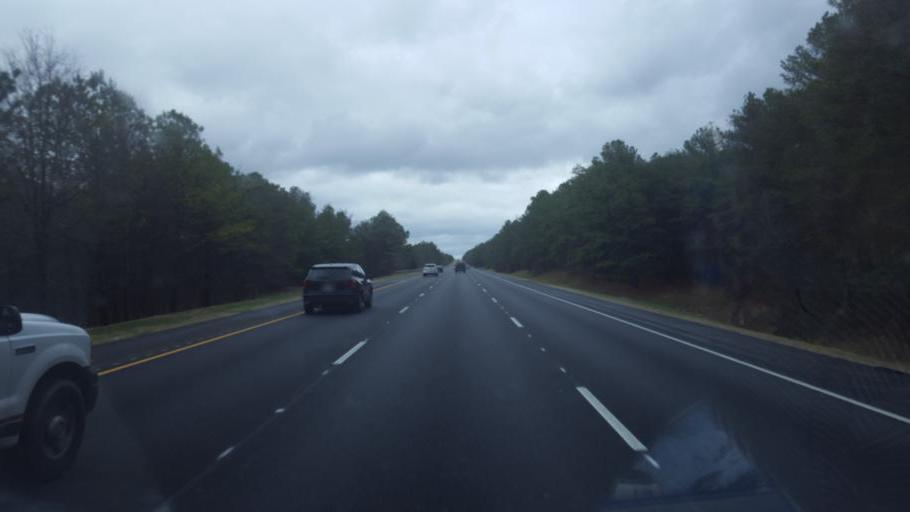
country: US
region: Georgia
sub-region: Whitfield County
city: Dalton
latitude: 34.8244
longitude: -85.0170
